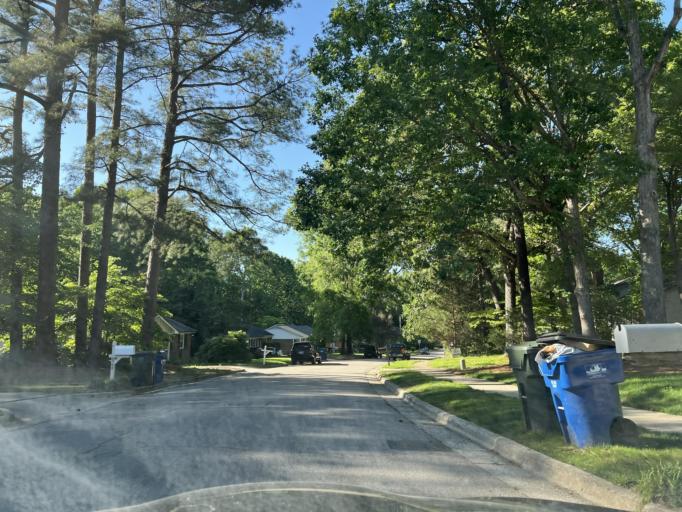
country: US
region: North Carolina
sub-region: Wake County
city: West Raleigh
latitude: 35.8599
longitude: -78.6421
